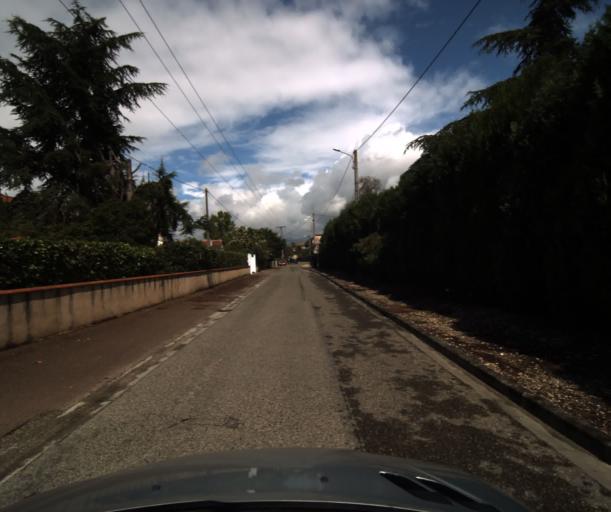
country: FR
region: Midi-Pyrenees
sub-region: Departement du Tarn-et-Garonne
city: Lavit
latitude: 43.9530
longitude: 0.9216
